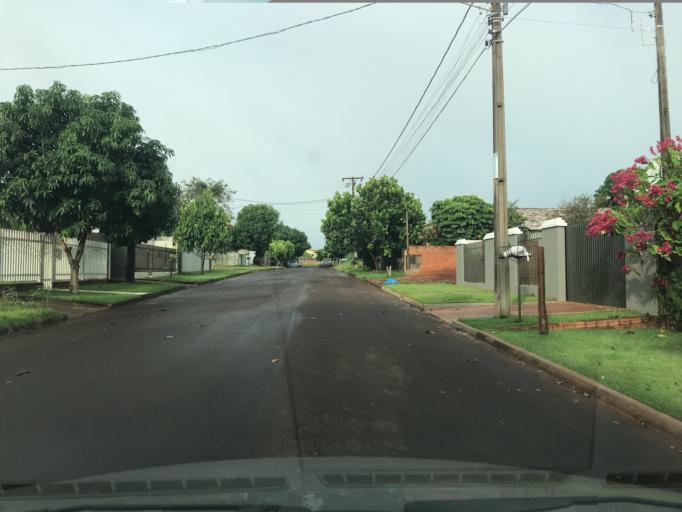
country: BR
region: Parana
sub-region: Palotina
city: Palotina
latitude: -24.3009
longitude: -53.8375
